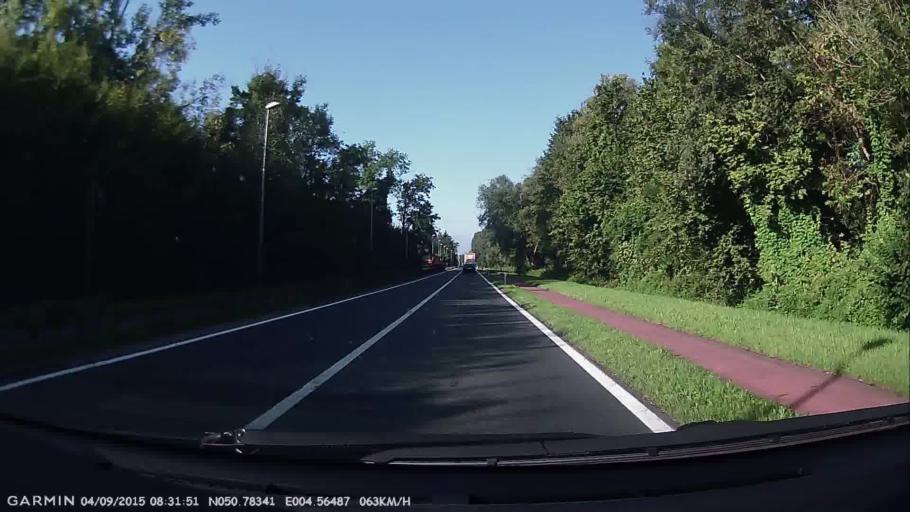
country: BE
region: Flanders
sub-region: Provincie Vlaams-Brabant
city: Huldenberg
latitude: 50.7832
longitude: 4.5644
